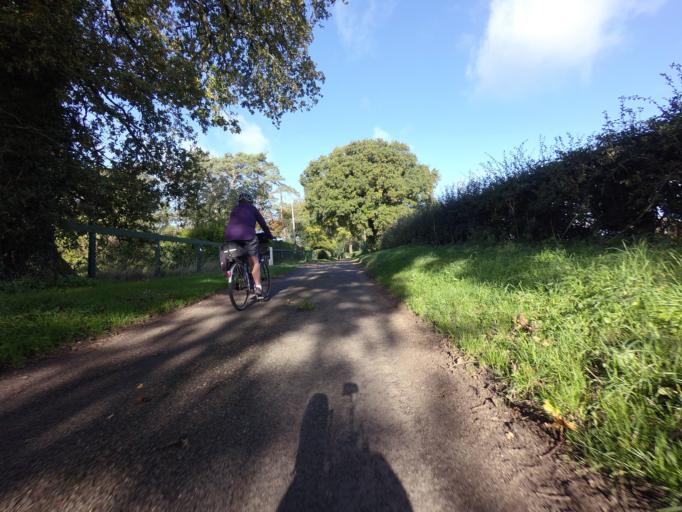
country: GB
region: England
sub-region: Norfolk
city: Fakenham
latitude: 52.8452
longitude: 0.6801
